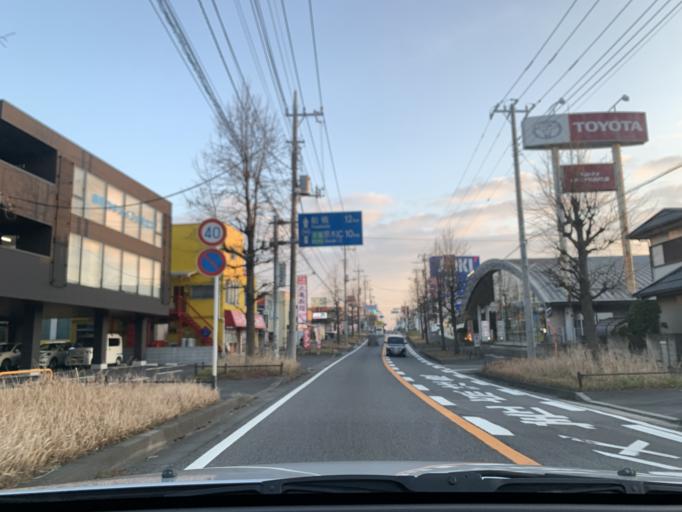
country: JP
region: Chiba
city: Matsudo
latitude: 35.7686
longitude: 139.9104
